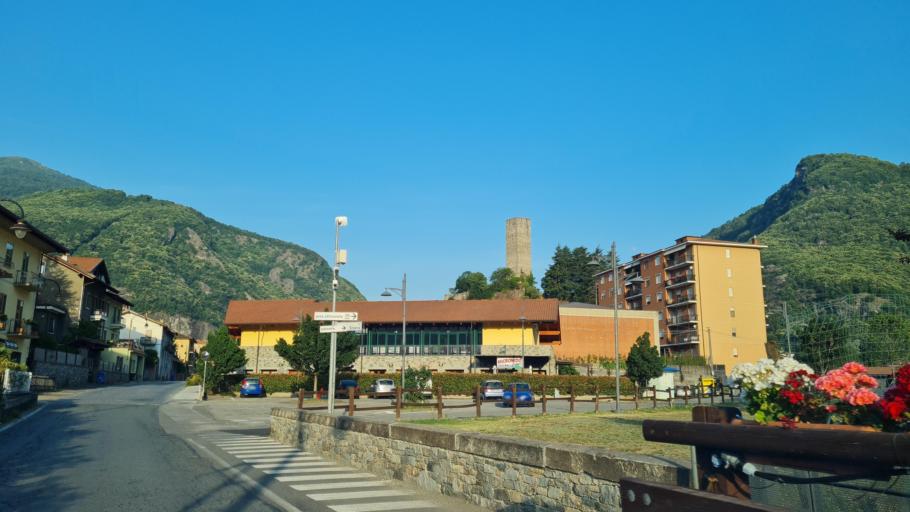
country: IT
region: Piedmont
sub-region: Provincia di Torino
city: Pont-Canavese
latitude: 45.4215
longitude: 7.6011
